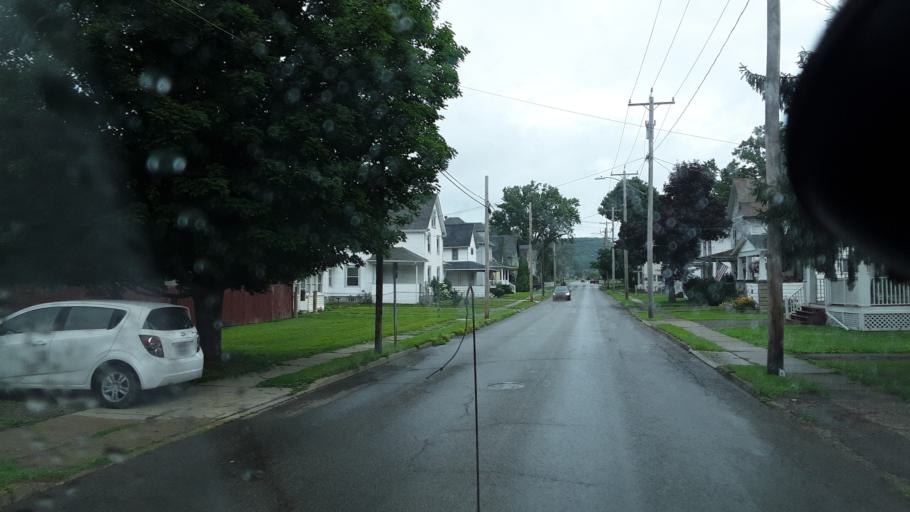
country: US
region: New York
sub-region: Cattaraugus County
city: Olean
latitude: 42.0816
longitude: -78.4447
